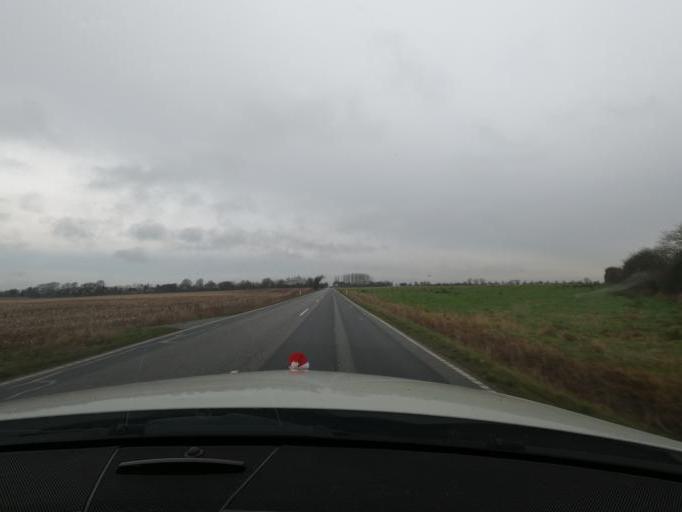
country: DK
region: South Denmark
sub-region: Haderslev Kommune
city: Starup
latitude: 55.1980
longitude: 9.5334
